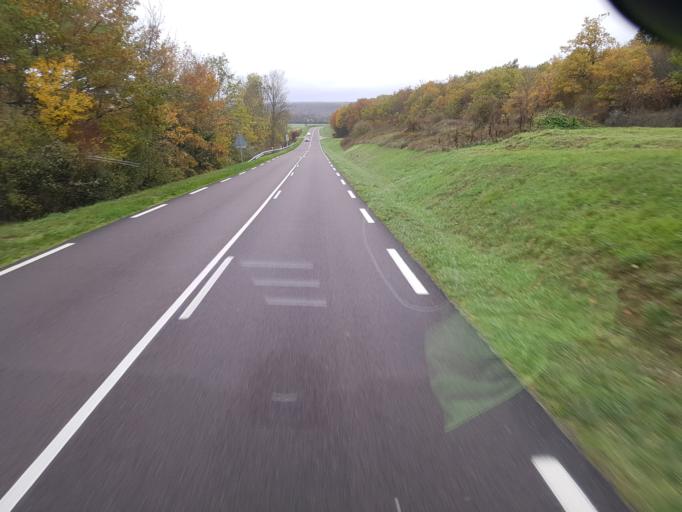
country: FR
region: Bourgogne
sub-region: Departement de la Cote-d'Or
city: Is-sur-Tille
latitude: 47.5251
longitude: 4.9996
